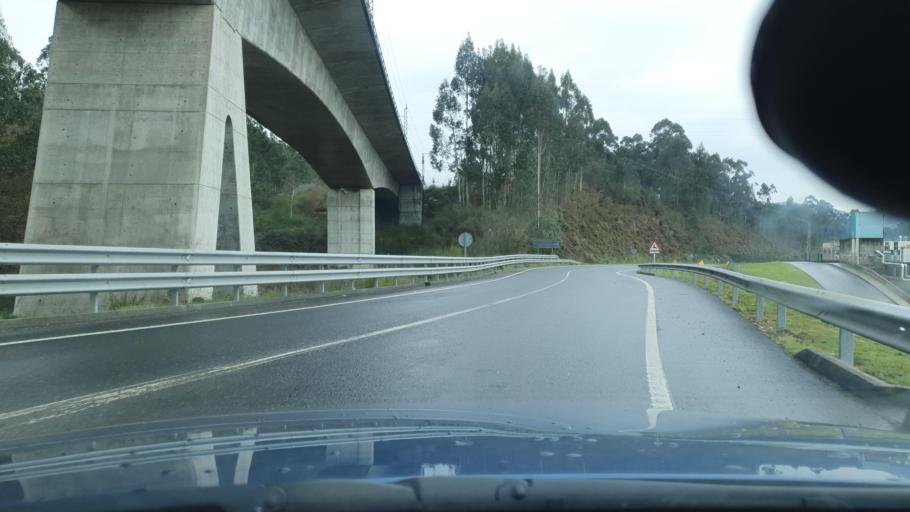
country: ES
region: Galicia
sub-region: Provincia da Coruna
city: Padron
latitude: 42.7555
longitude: -8.6776
